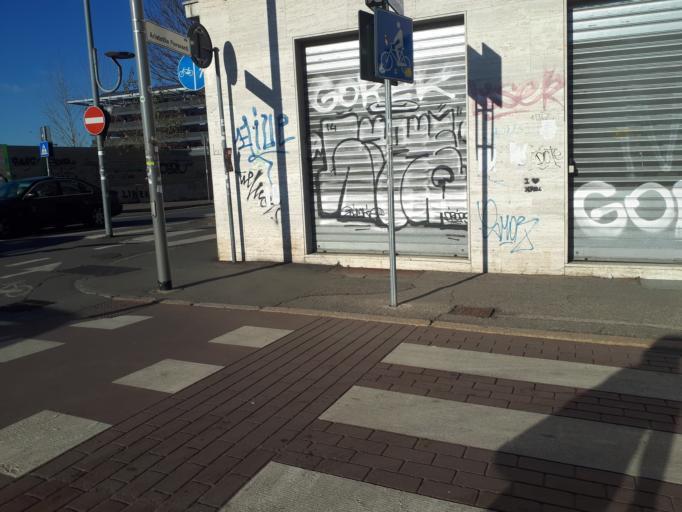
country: IT
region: Emilia-Romagna
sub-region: Provincia di Bologna
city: Bologna
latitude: 44.5078
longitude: 11.3404
